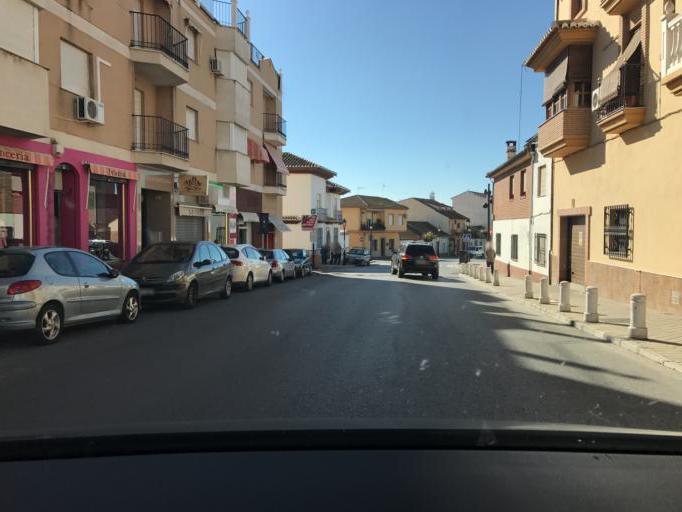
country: ES
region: Andalusia
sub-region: Provincia de Granada
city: Atarfe
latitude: 37.2220
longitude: -3.6856
